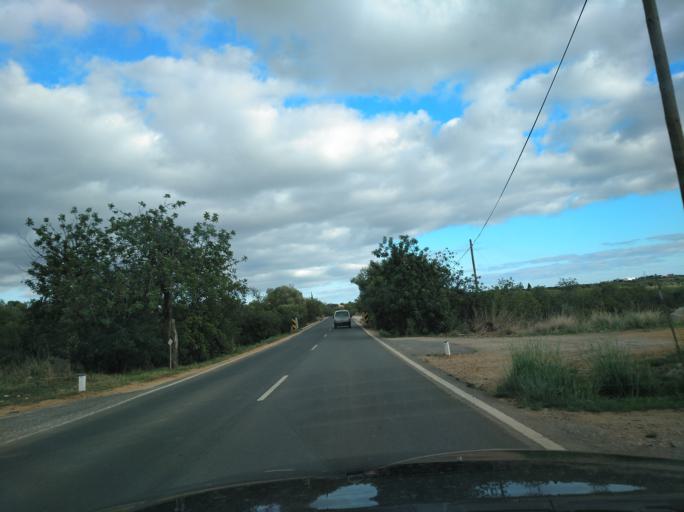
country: PT
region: Faro
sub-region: Tavira
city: Luz
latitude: 37.1387
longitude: -7.7065
